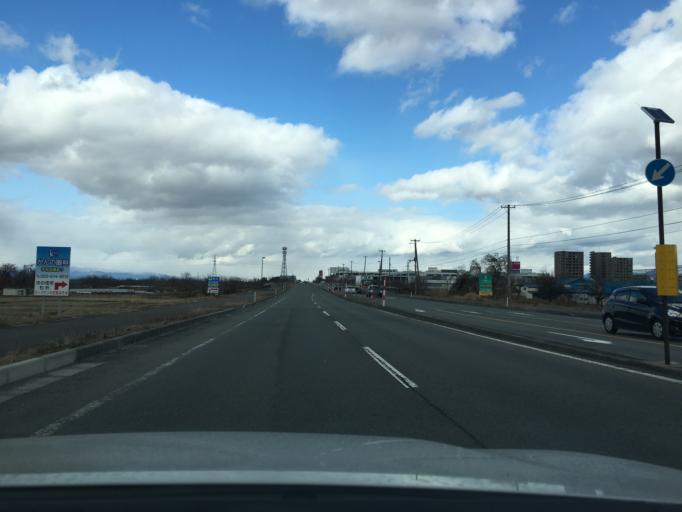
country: JP
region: Yamagata
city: Yamagata-shi
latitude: 38.2208
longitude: 140.3024
